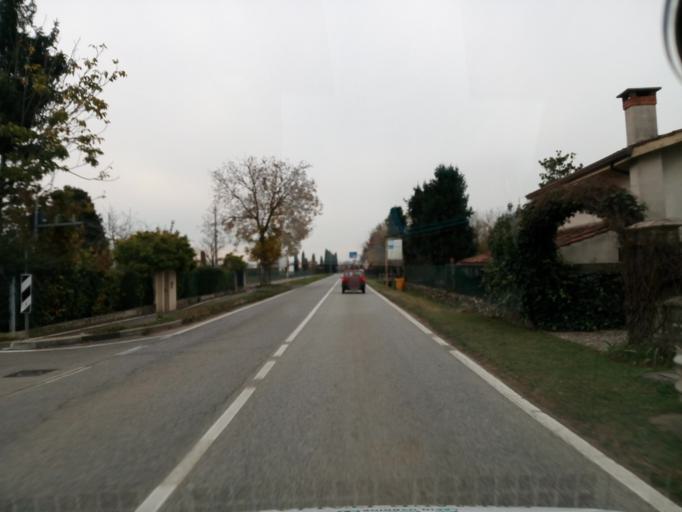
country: IT
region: Veneto
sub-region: Provincia di Treviso
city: Vedelago
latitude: 45.6953
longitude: 12.0174
